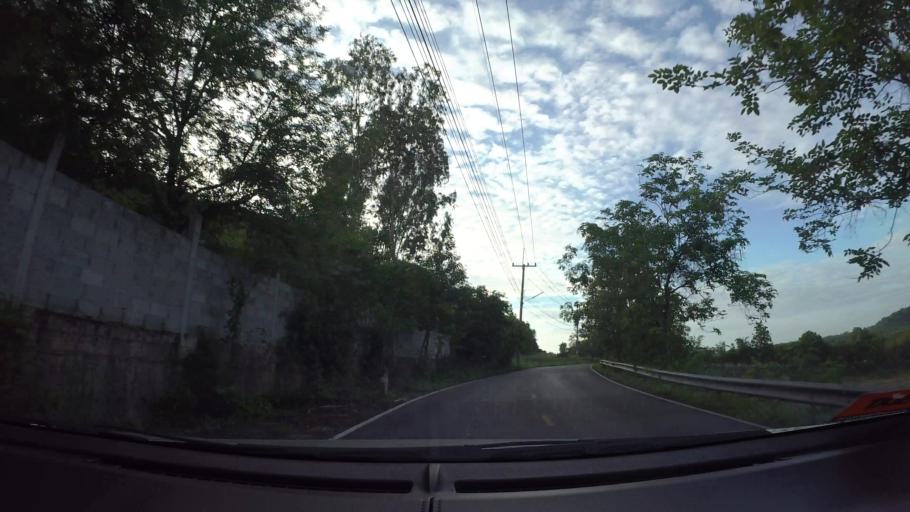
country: TH
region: Chon Buri
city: Sattahip
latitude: 12.7446
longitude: 100.9339
